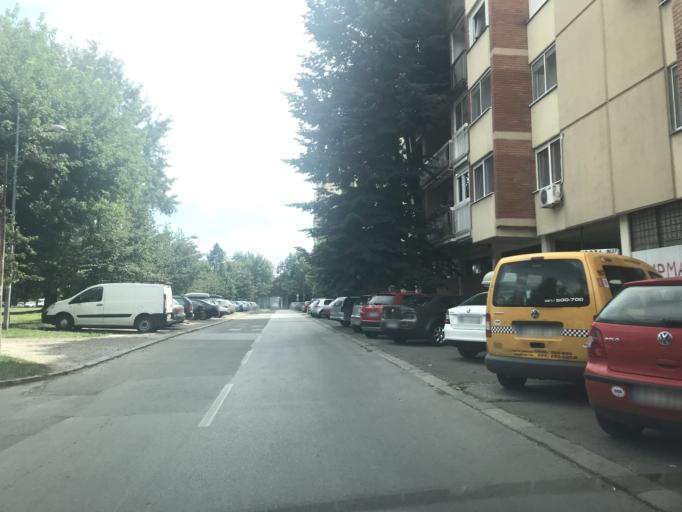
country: RS
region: Autonomna Pokrajina Vojvodina
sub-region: Juznobacki Okrug
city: Novi Sad
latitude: 45.2370
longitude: 19.8293
